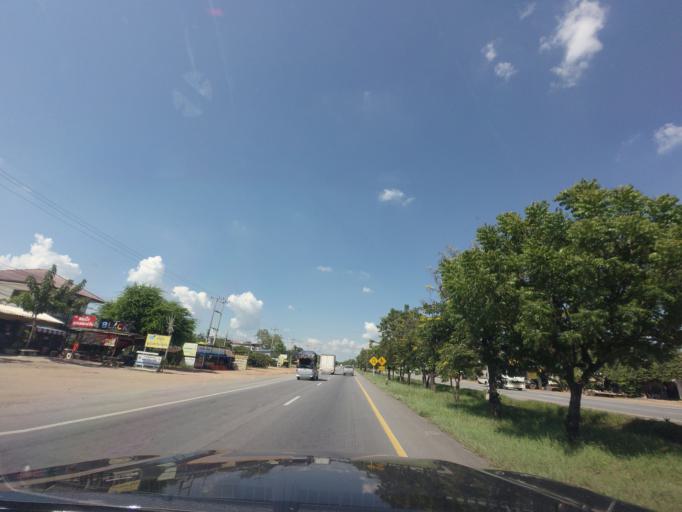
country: TH
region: Nakhon Ratchasima
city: Non Sung
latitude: 15.1676
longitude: 102.3336
